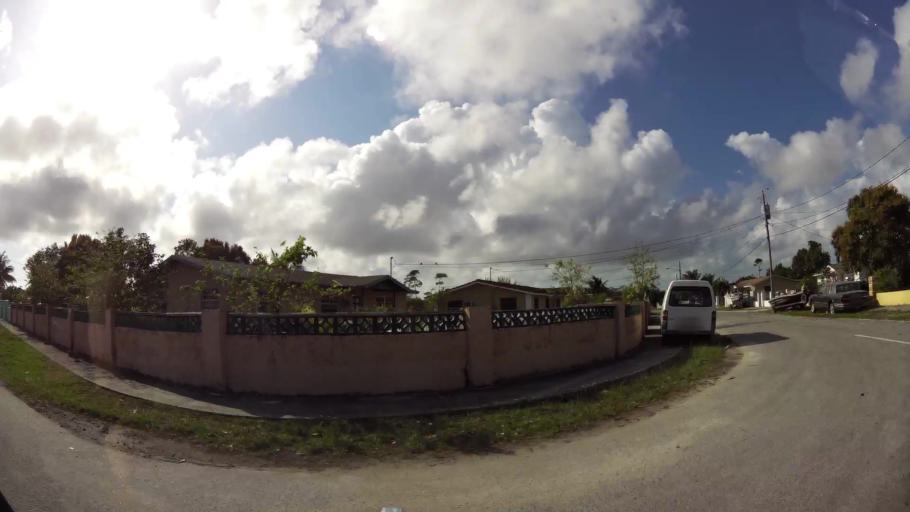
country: BS
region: Freeport
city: Lucaya
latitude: 26.5305
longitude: -78.6721
